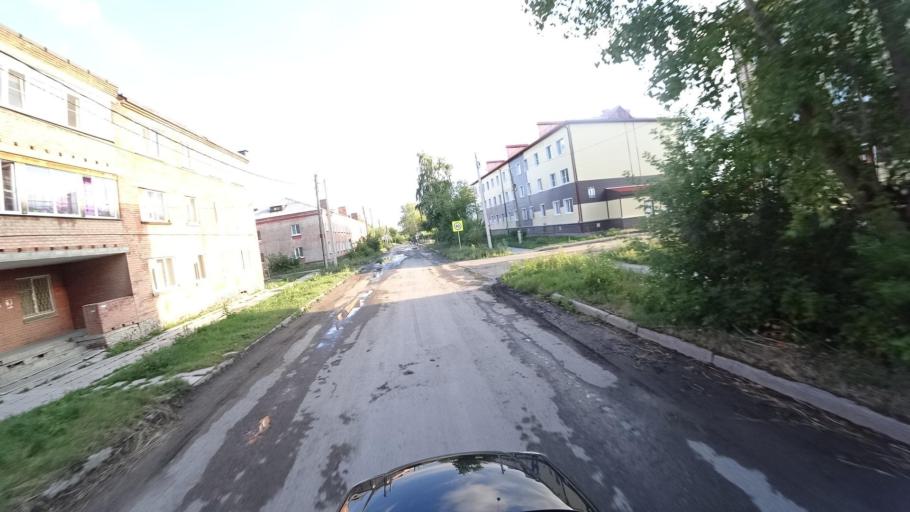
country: RU
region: Sverdlovsk
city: Kamyshlov
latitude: 56.8523
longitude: 62.7280
